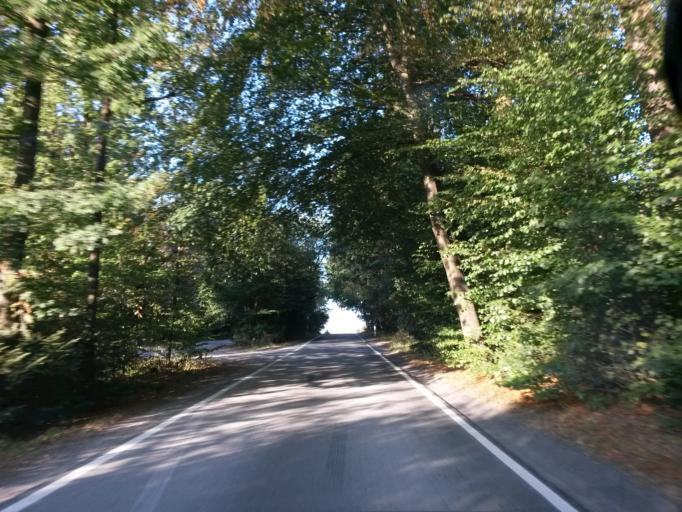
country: DE
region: North Rhine-Westphalia
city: Wipperfurth
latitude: 51.0929
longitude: 7.4118
